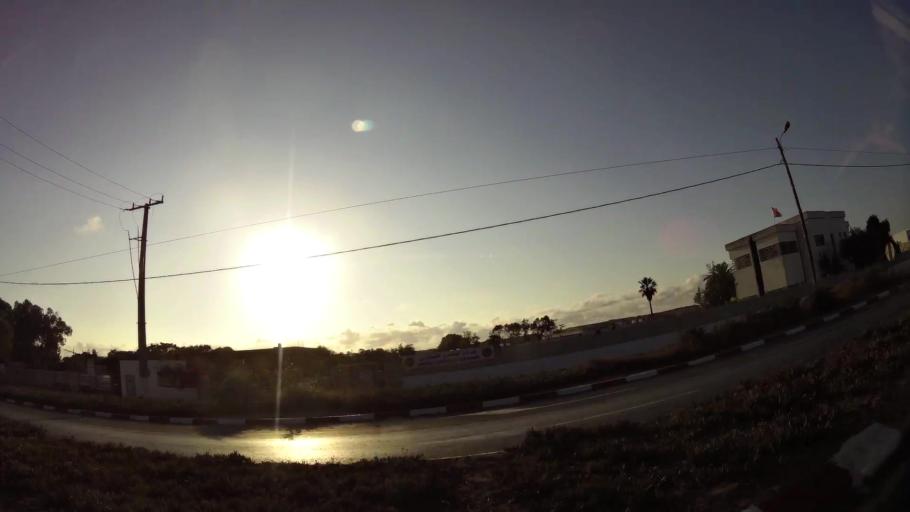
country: MA
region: Rabat-Sale-Zemmour-Zaer
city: Sale
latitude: 34.0946
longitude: -6.7639
